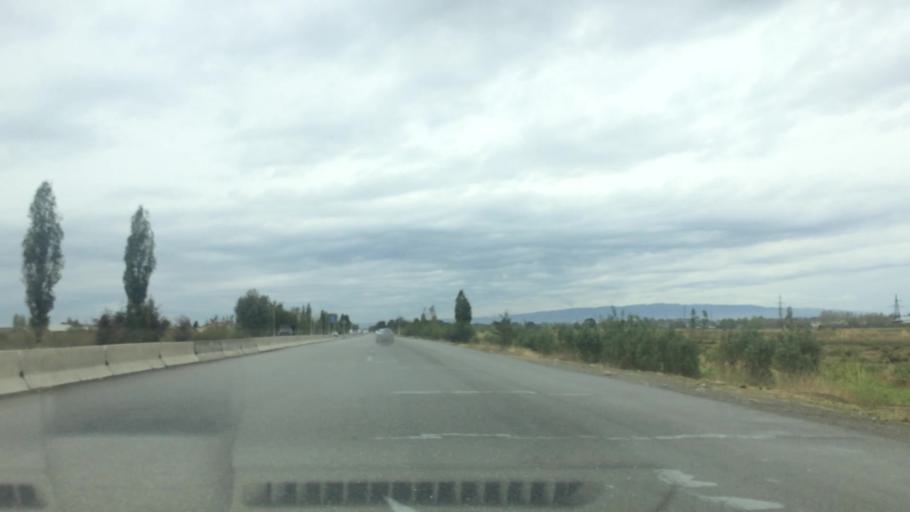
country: UZ
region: Jizzax
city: Jizzax
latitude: 40.0204
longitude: 67.6124
